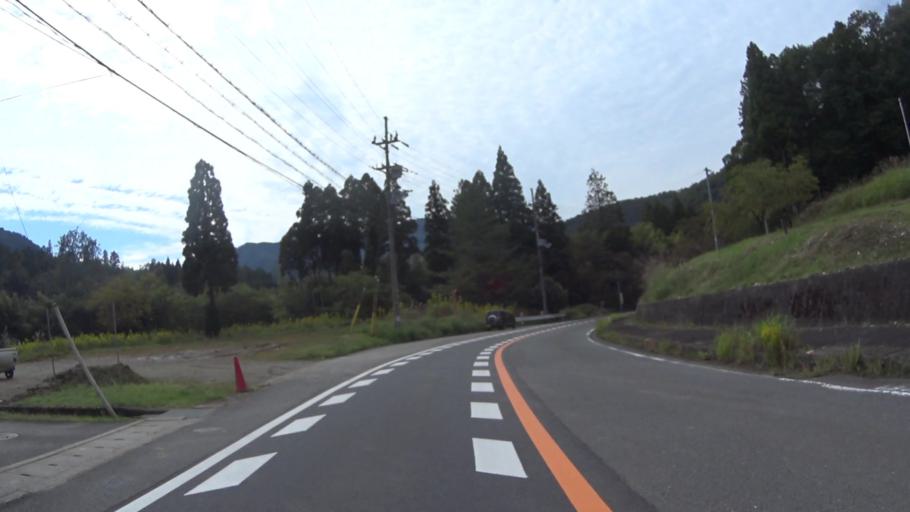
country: JP
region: Kyoto
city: Maizuru
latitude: 35.2711
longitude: 135.5014
